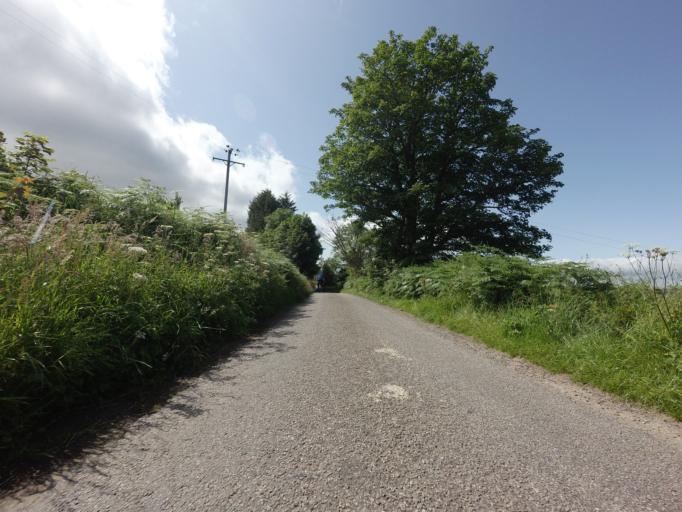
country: GB
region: Scotland
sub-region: Highland
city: Fortrose
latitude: 57.4893
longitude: -4.0190
